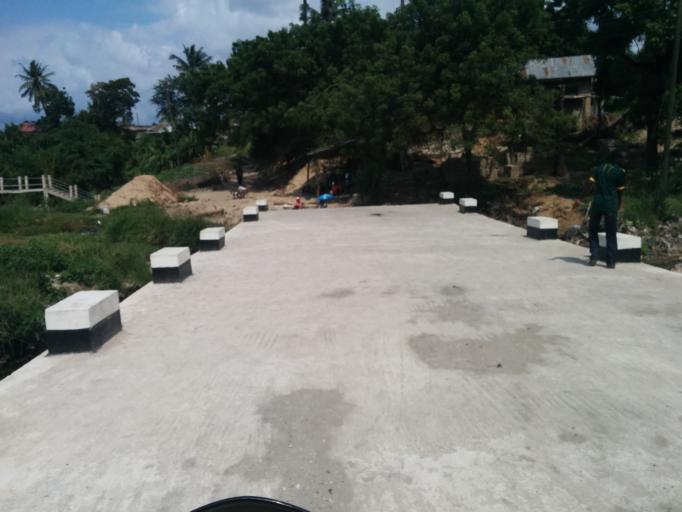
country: TZ
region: Dar es Salaam
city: Dar es Salaam
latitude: -6.8638
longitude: 39.2467
